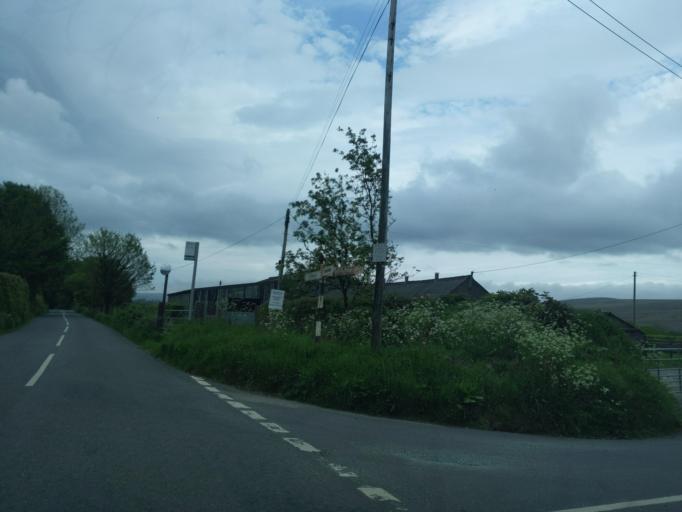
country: GB
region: England
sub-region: Devon
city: Tavistock
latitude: 50.6108
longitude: -4.1575
